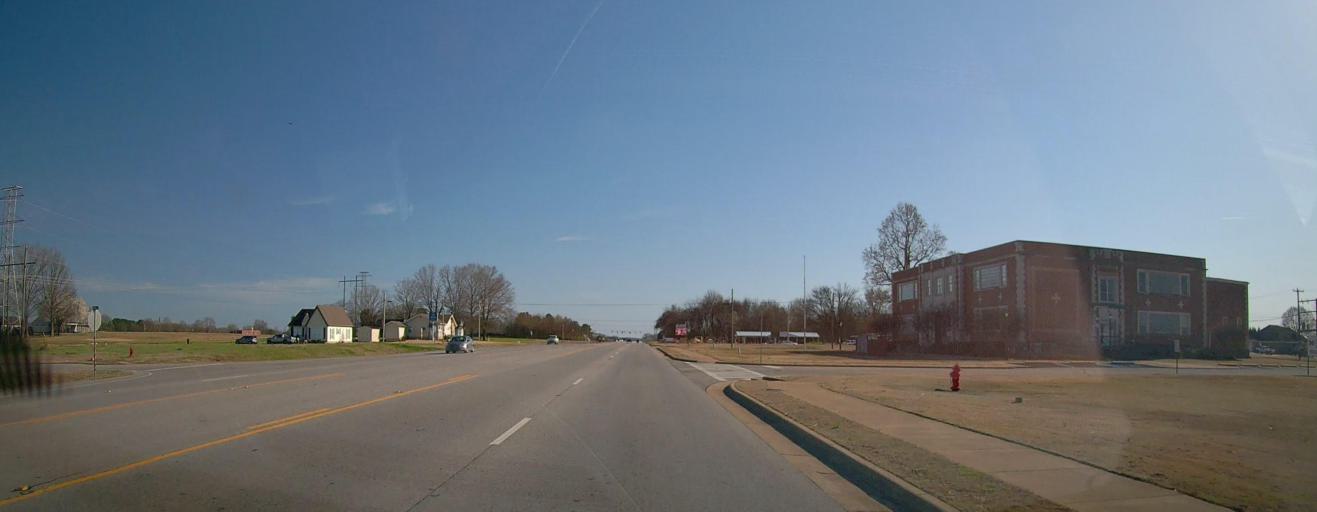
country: US
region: Alabama
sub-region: Colbert County
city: Muscle Shoals
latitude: 34.7343
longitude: -87.6353
